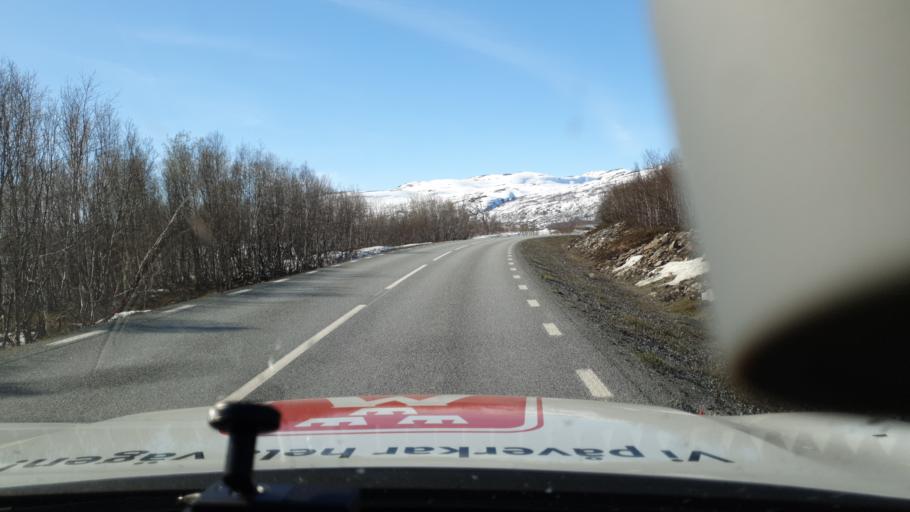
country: NO
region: Nordland
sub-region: Rana
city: Mo i Rana
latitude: 66.1023
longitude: 14.8229
